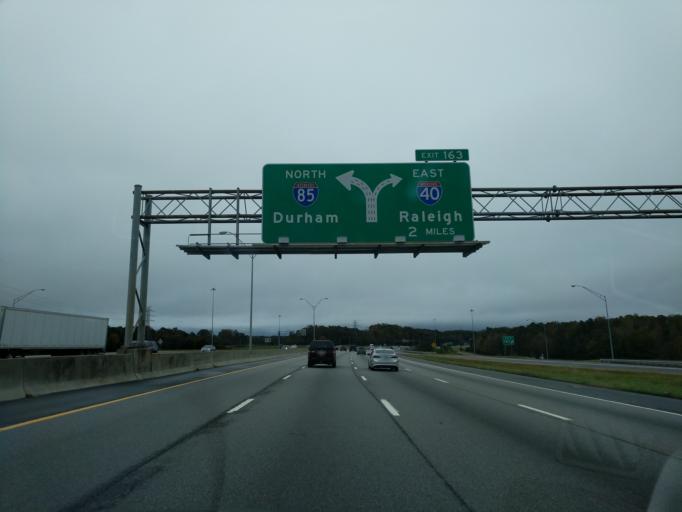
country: US
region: North Carolina
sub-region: Orange County
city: Hillsborough
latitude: 36.0733
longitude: -79.1647
